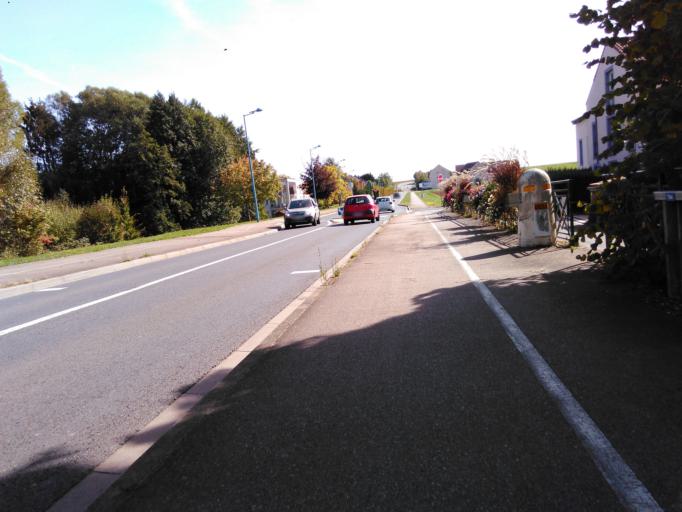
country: FR
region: Lorraine
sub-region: Departement de la Moselle
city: Hettange-Grande
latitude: 49.3965
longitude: 6.1637
